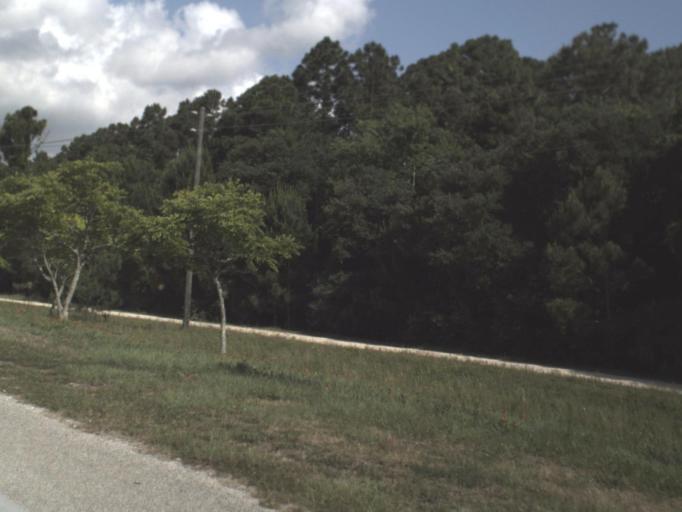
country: US
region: Florida
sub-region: Saint Johns County
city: Saint Augustine South
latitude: 29.8672
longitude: -81.3011
